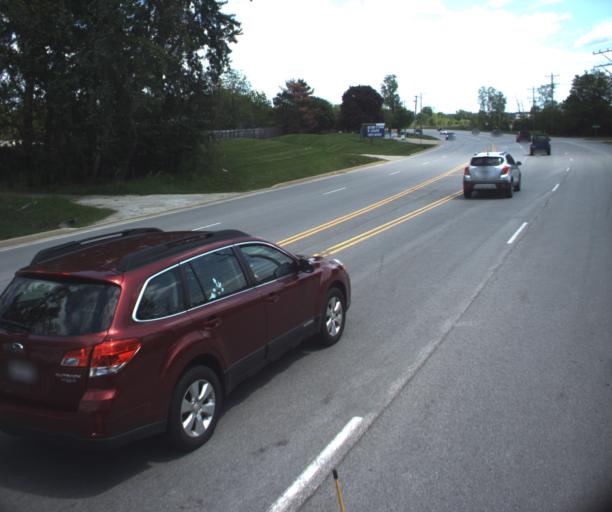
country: US
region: Illinois
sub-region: Kane County
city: Geneva
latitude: 41.8690
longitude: -88.2732
